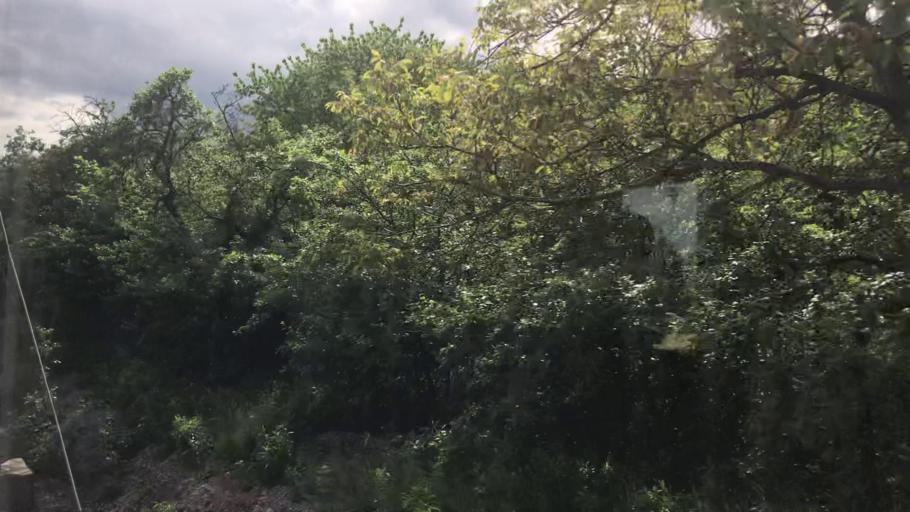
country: PL
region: Lower Silesian Voivodeship
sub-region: Powiat swidnicki
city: Swiebodzice
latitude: 50.8572
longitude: 16.3442
